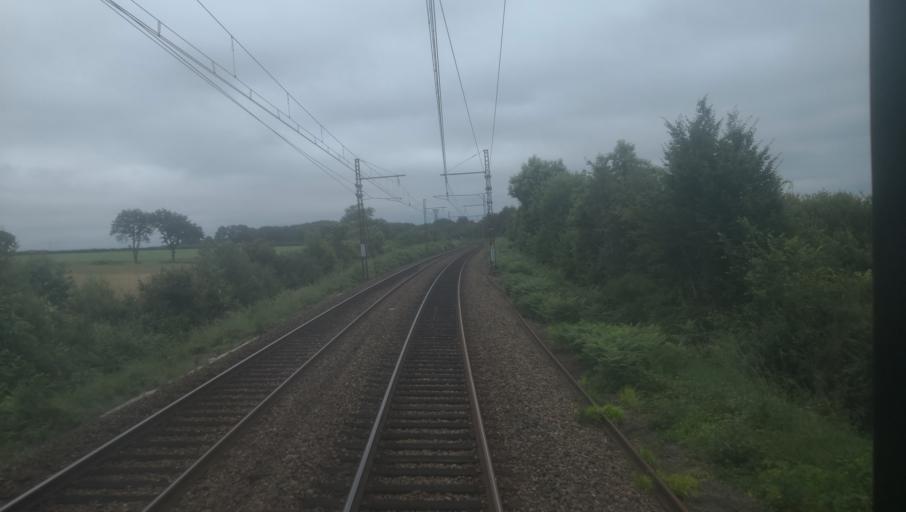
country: FR
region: Centre
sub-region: Departement de l'Indre
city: Chantome
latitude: 46.4756
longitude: 1.5353
